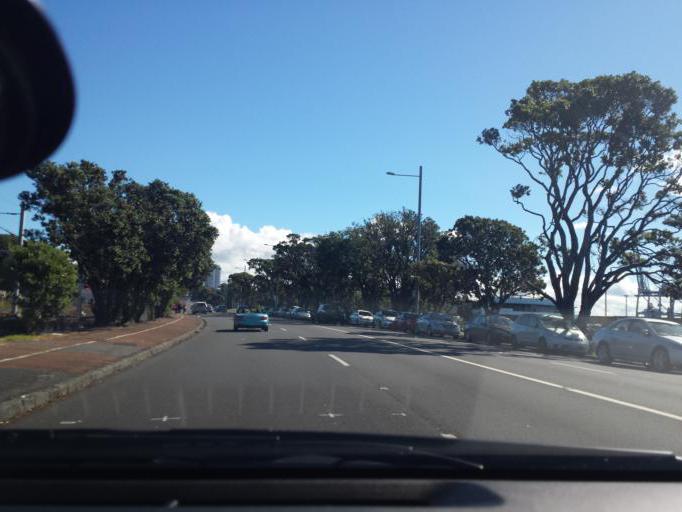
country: NZ
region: Auckland
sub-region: Auckland
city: Auckland
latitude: -36.8479
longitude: 174.7907
